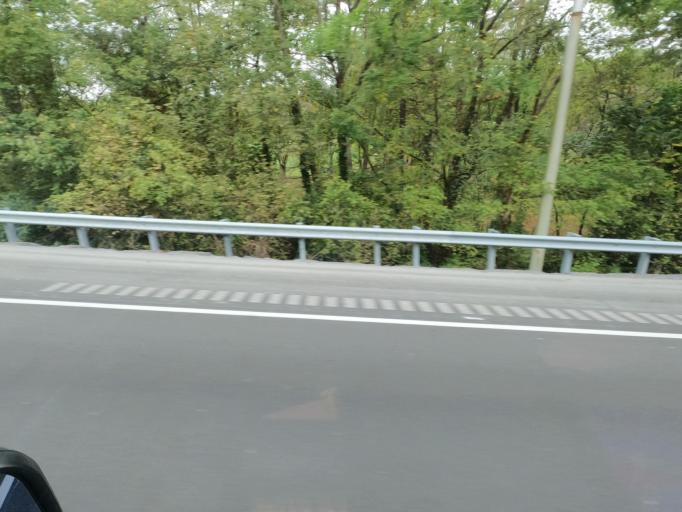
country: US
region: Tennessee
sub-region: Sullivan County
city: Colonial Heights
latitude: 36.5335
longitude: -82.5032
